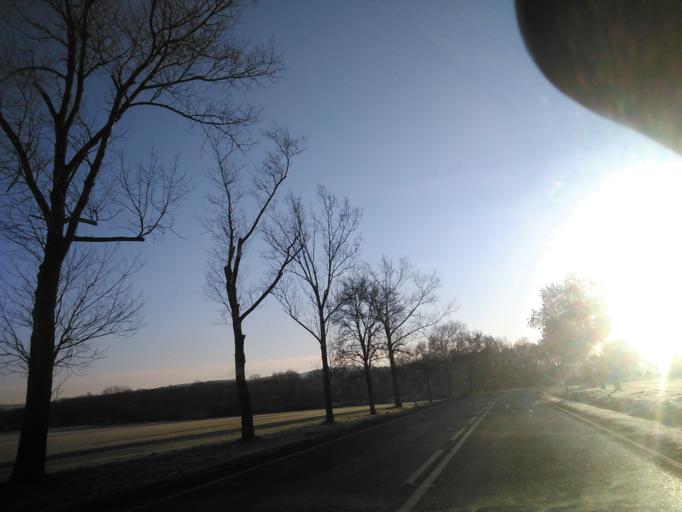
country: PL
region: Lower Silesian Voivodeship
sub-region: Powiat jaworski
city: Bolkow
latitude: 50.9120
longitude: 16.1354
